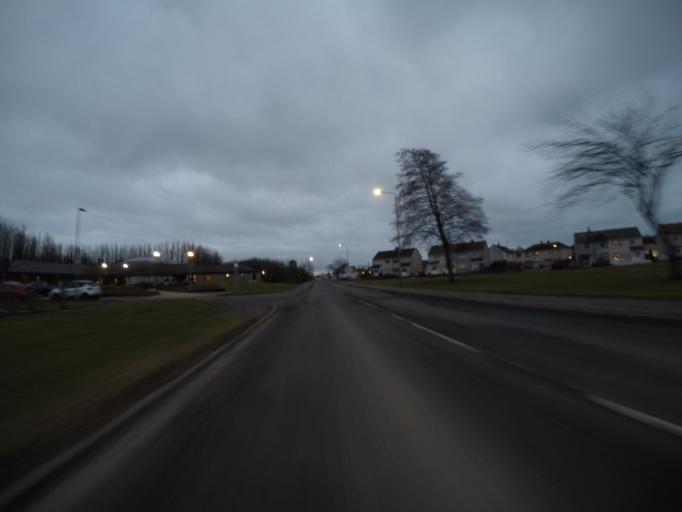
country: GB
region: Scotland
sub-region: North Ayrshire
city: Kilwinning
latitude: 55.6496
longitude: -4.6986
